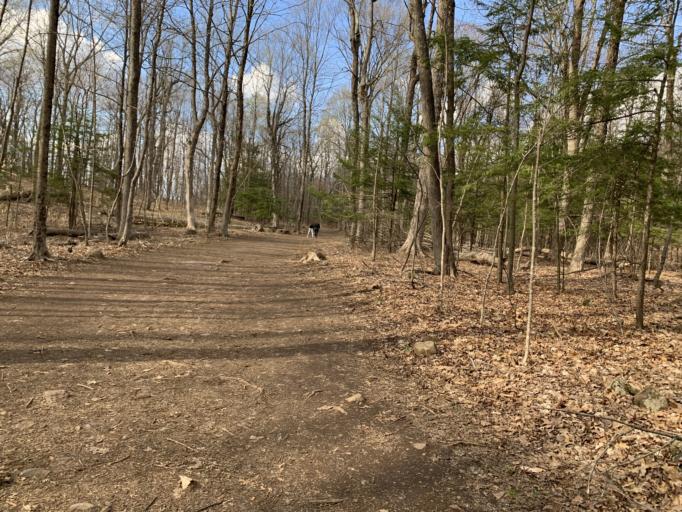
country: US
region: Connecticut
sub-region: Hartford County
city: Weatogue
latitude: 41.8334
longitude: -72.7975
